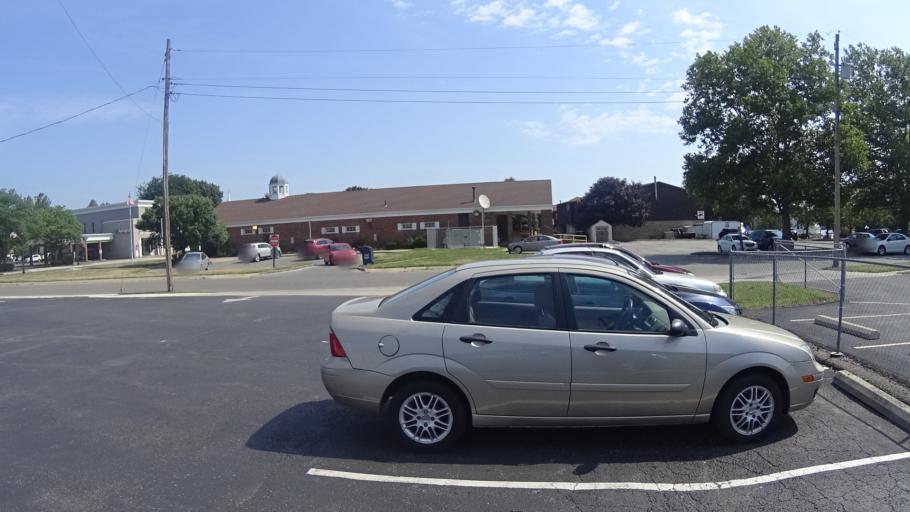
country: US
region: Ohio
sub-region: Erie County
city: Huron
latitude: 41.3922
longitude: -82.5561
